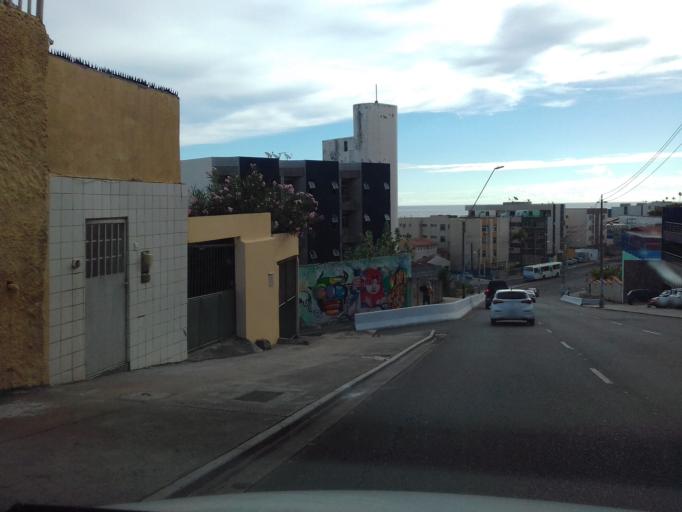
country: BR
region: Bahia
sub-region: Salvador
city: Salvador
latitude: -13.0123
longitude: -38.4738
